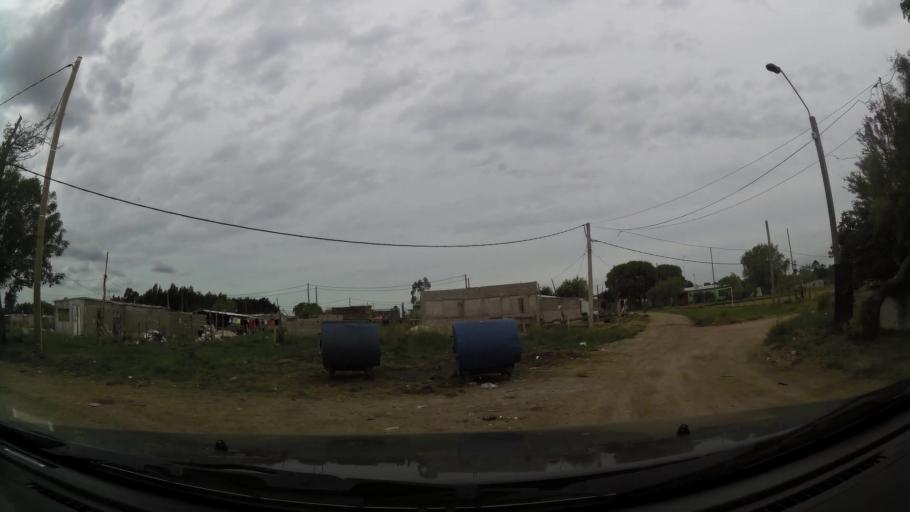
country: UY
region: Canelones
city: Las Piedras
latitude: -34.7110
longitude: -56.2029
